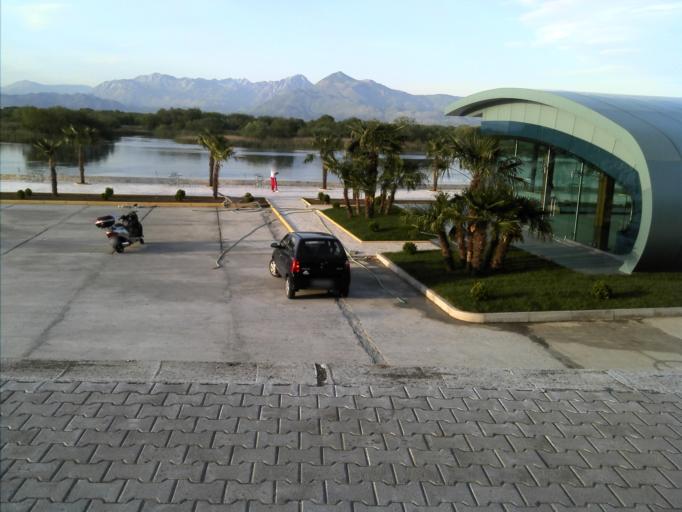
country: AL
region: Shkoder
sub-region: Rrethi i Shkodres
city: Shkoder
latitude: 42.0543
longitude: 19.4775
